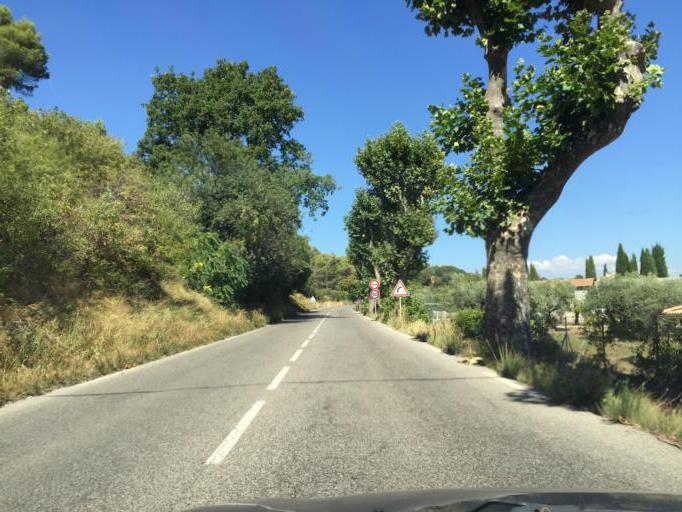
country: FR
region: Provence-Alpes-Cote d'Azur
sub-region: Departement des Alpes-de-Haute-Provence
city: Peyruis
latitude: 44.0219
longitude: 5.9303
